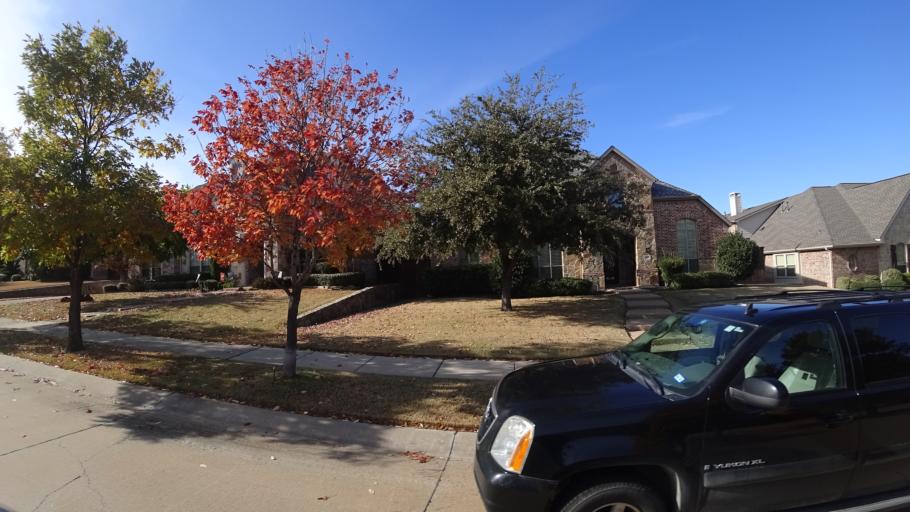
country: US
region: Texas
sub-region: Denton County
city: The Colony
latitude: 33.0278
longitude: -96.9074
